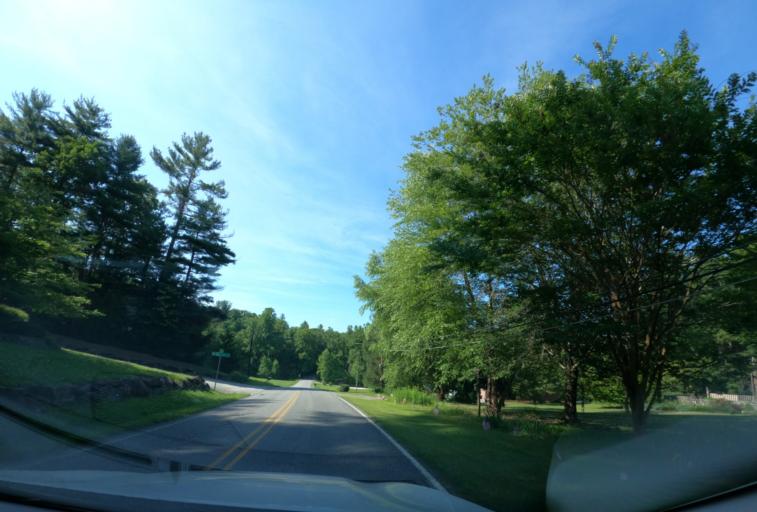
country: US
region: North Carolina
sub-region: Henderson County
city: Etowah
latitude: 35.2419
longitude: -82.6430
